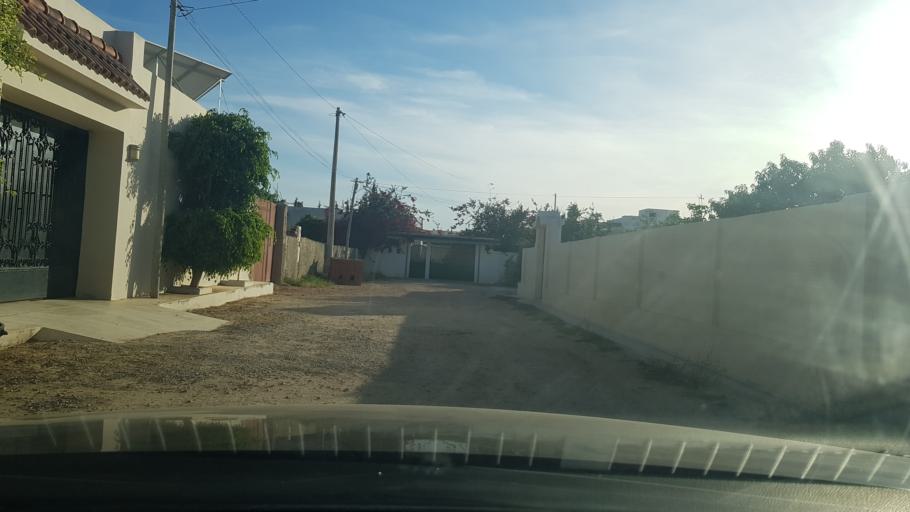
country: TN
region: Safaqis
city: Al Qarmadah
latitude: 34.8309
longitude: 10.7613
